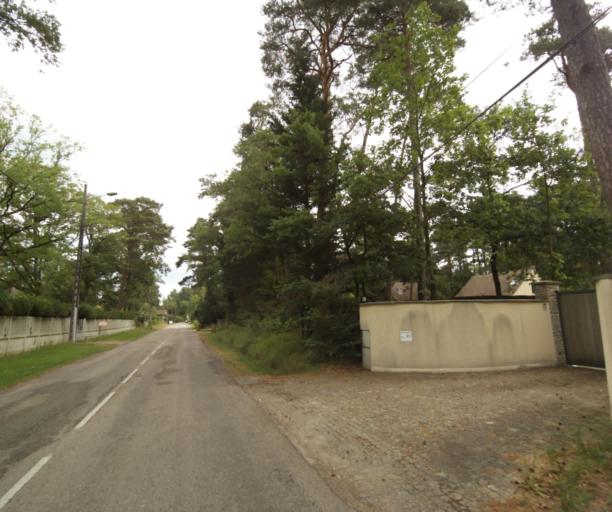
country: FR
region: Ile-de-France
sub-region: Departement de Seine-et-Marne
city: Arbonne-la-Foret
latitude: 48.4056
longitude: 2.5617
